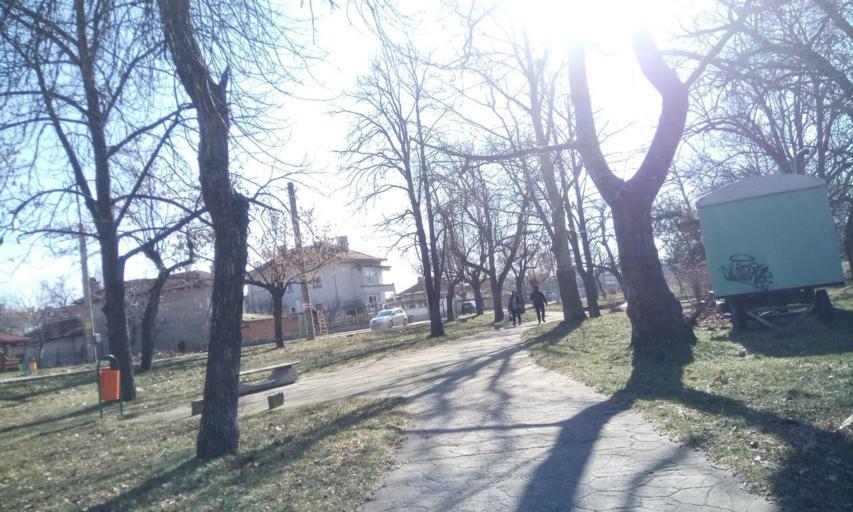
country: BG
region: Plovdiv
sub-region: Obshtina Khisarya
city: Khisarya
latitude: 42.5107
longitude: 24.7150
